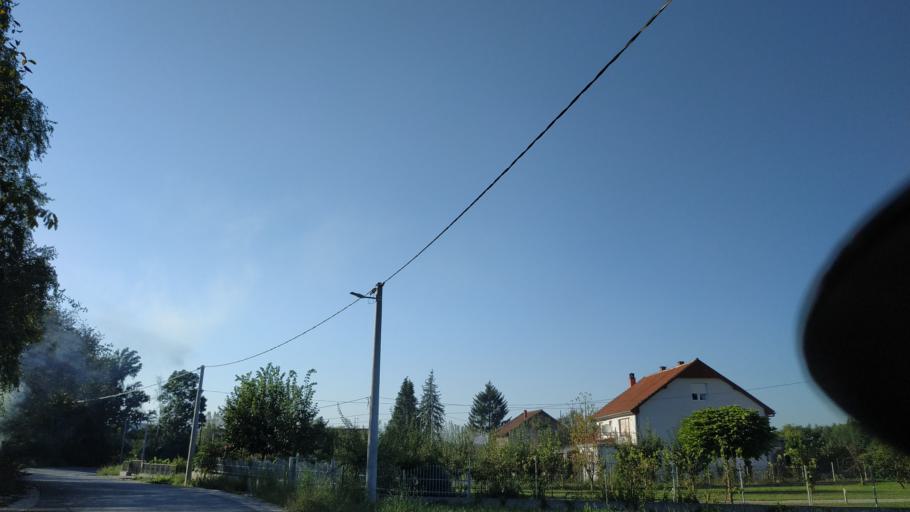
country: RS
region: Central Serbia
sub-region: Rasinski Okrug
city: Krusevac
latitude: 43.5082
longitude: 21.3320
